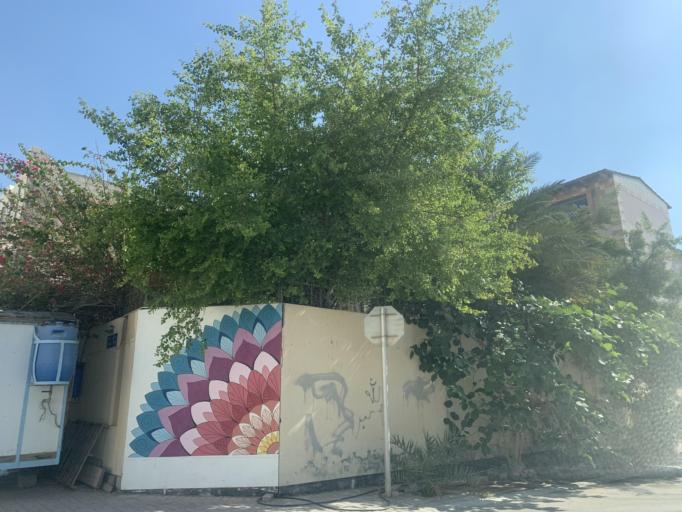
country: BH
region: Central Governorate
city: Madinat Hamad
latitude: 26.1236
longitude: 50.4953
